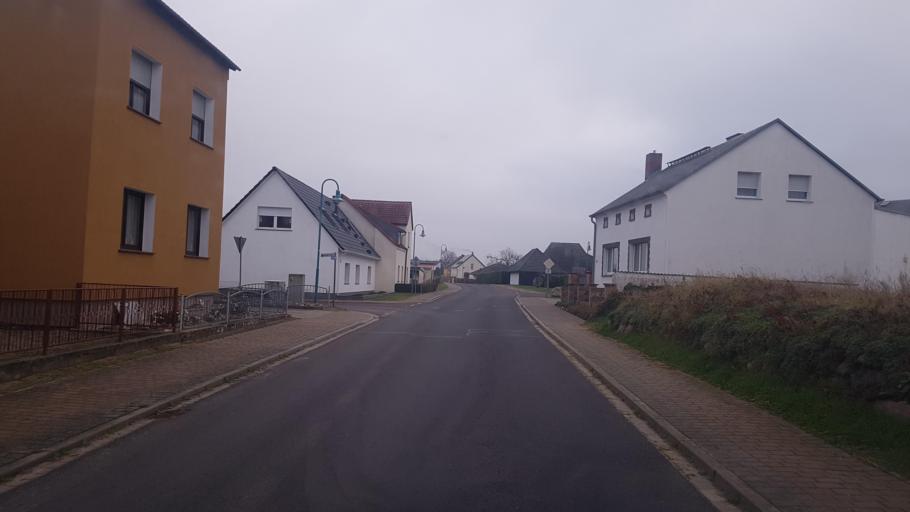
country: DE
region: Brandenburg
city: Gross Kreutz
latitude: 52.3802
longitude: 12.7941
